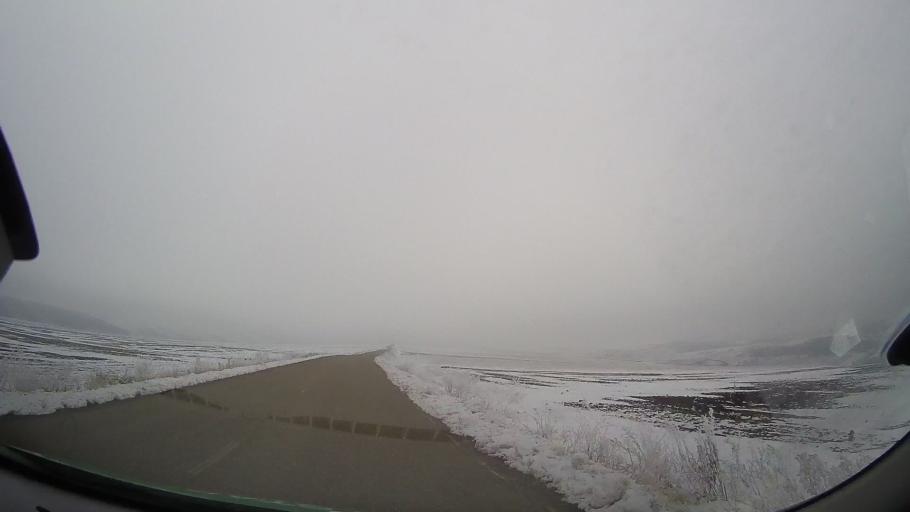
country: RO
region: Vaslui
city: Coroiesti
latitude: 46.2304
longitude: 27.4779
